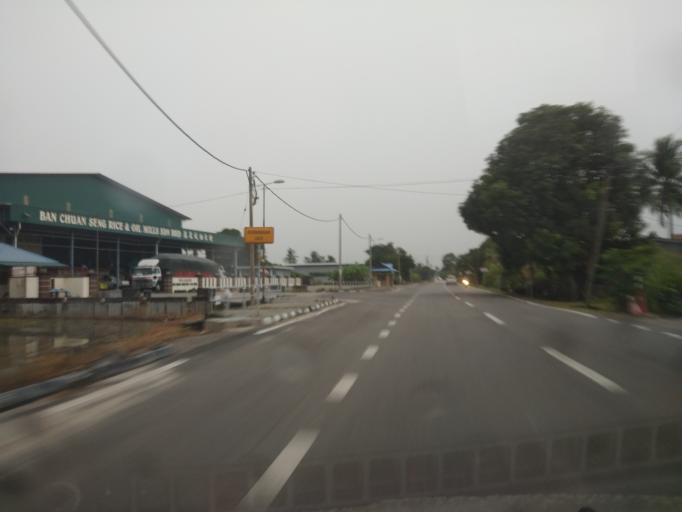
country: MY
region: Penang
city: Permatang Kuching
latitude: 5.4953
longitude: 100.3975
